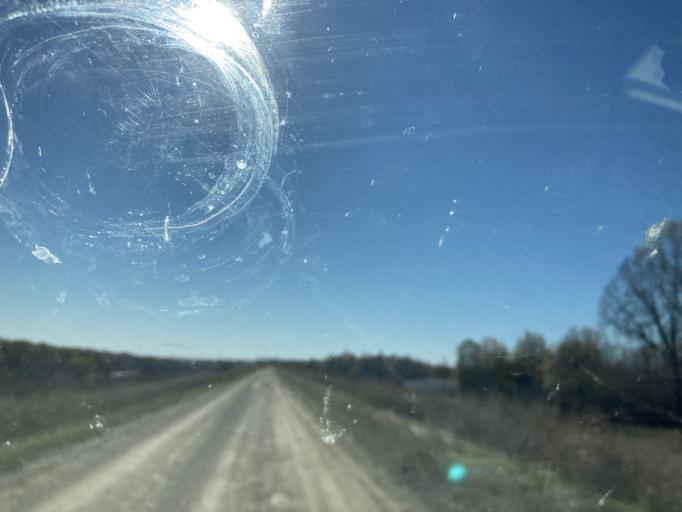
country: US
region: Mississippi
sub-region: Sharkey County
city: Rolling Fork
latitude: 32.7506
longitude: -90.6610
